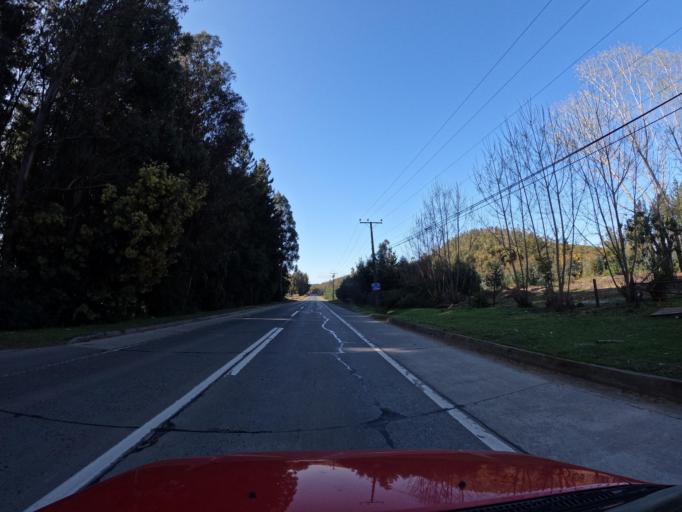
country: CL
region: Maule
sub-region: Provincia de Talca
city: Constitucion
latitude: -35.4311
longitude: -72.3348
